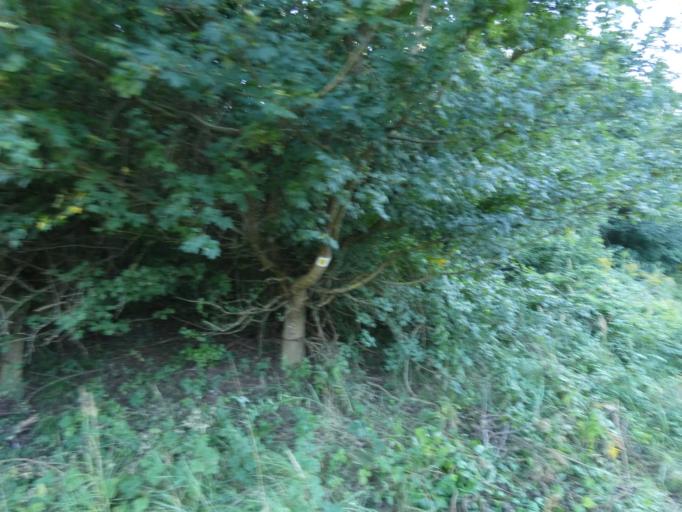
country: HU
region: Pest
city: Telki
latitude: 47.5808
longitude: 18.8552
